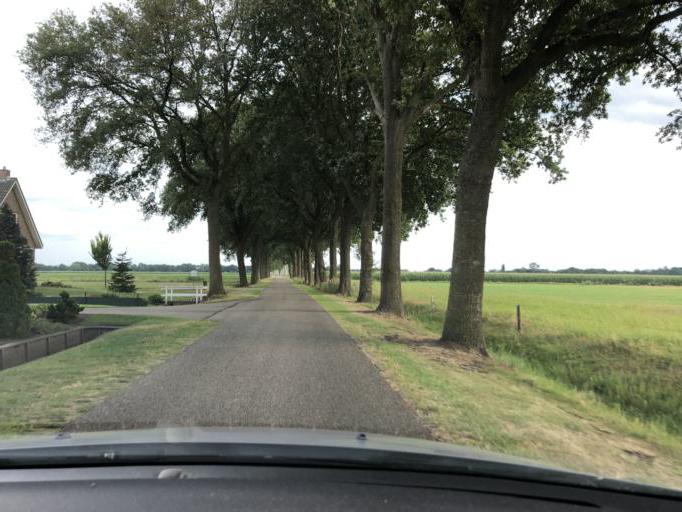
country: NL
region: Overijssel
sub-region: Gemeente Dalfsen
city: Dalfsen
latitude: 52.5917
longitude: 6.3154
